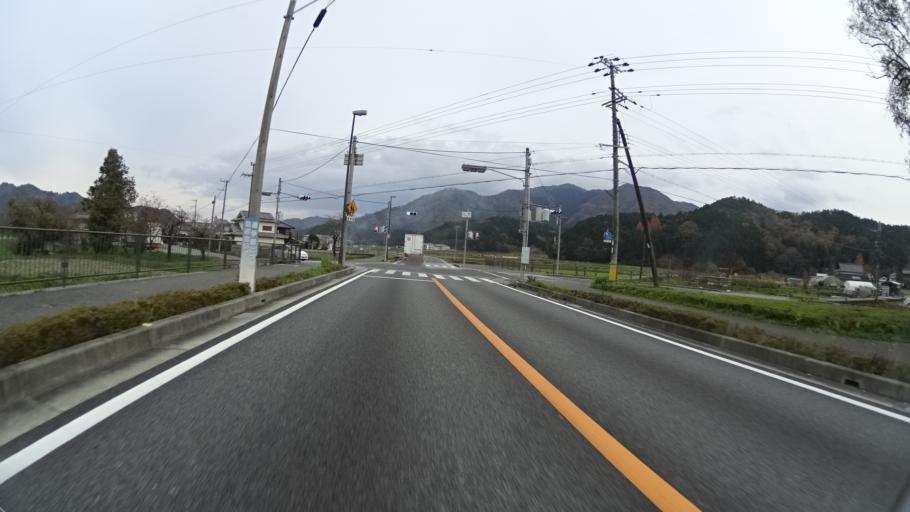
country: JP
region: Hyogo
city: Sasayama
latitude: 35.0685
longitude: 135.2872
